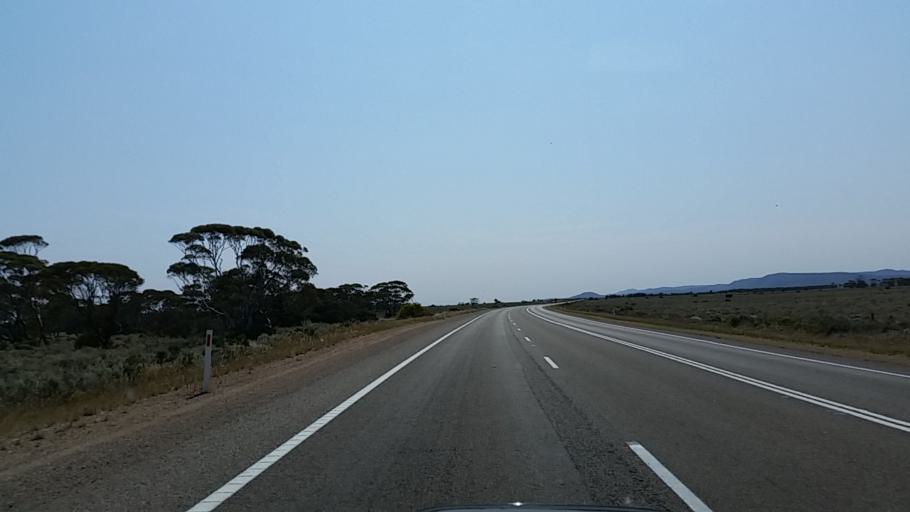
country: AU
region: South Australia
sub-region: Port Pirie City and Dists
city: Port Pirie
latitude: -32.9755
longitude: 137.9828
